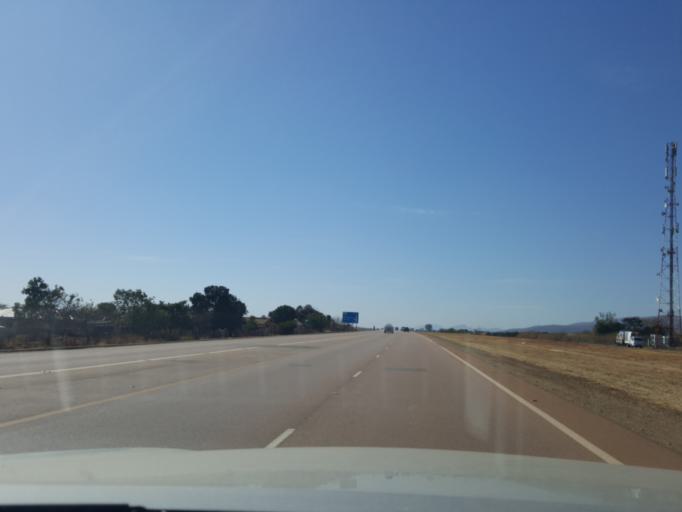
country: ZA
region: North-West
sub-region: Bojanala Platinum District Municipality
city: Brits
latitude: -25.7358
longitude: 27.6446
